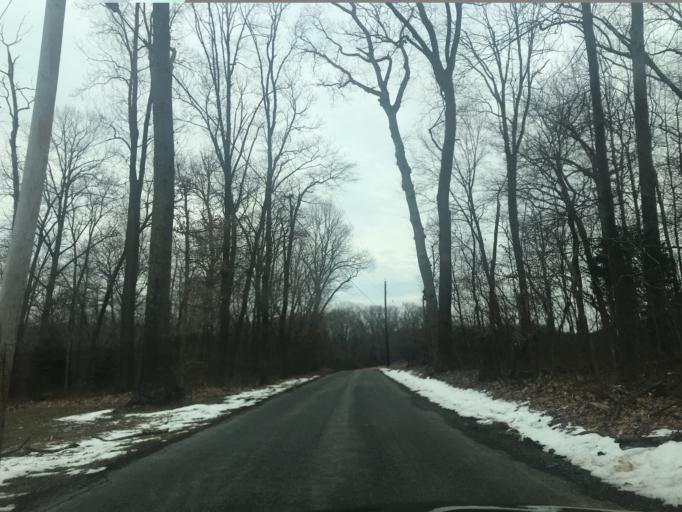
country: US
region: Pennsylvania
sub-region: York County
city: Stewartstown
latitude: 39.6946
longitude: -76.5287
